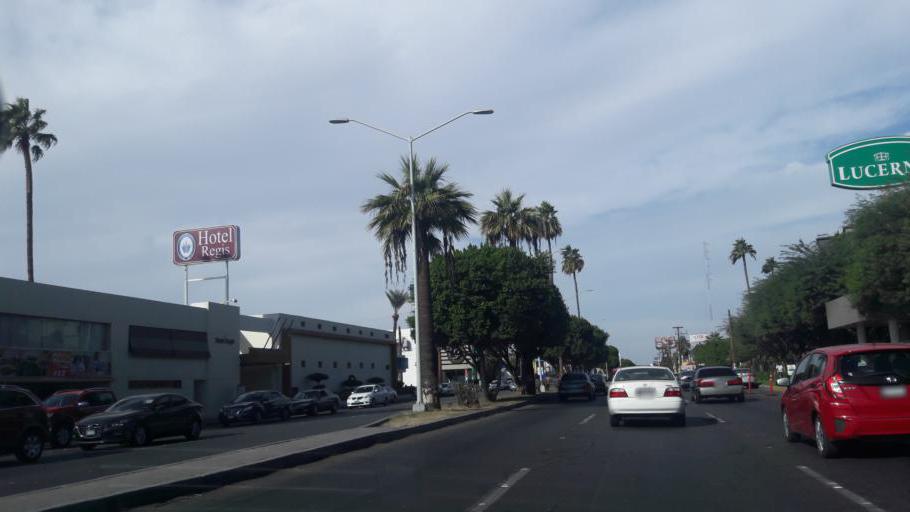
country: MX
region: Baja California
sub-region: Mexicali
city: Mexicali
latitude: 32.6381
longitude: -115.4487
